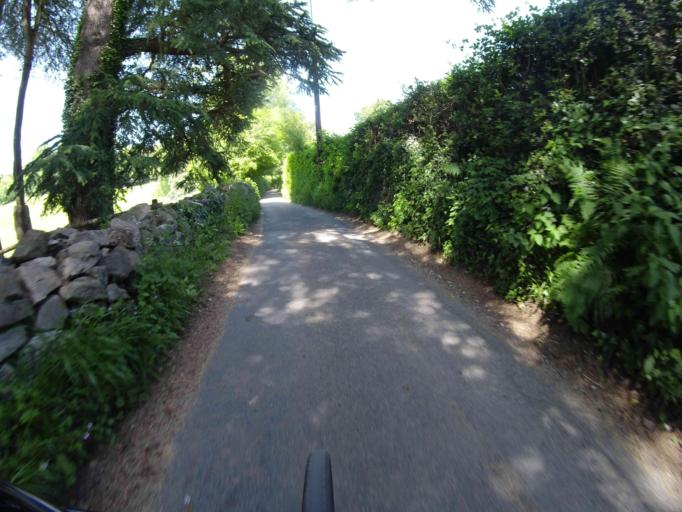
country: GB
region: England
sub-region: Devon
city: Bovey Tracey
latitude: 50.6099
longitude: -3.7099
